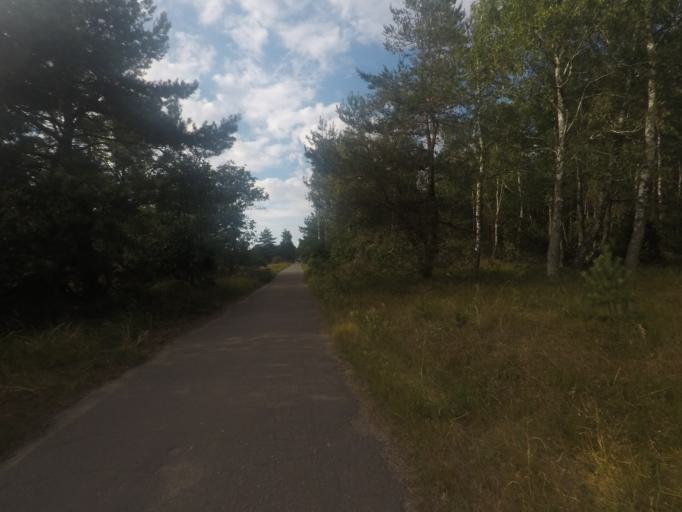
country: LT
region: Klaipedos apskritis
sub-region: Klaipeda
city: Klaipeda
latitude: 55.6840
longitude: 21.1041
